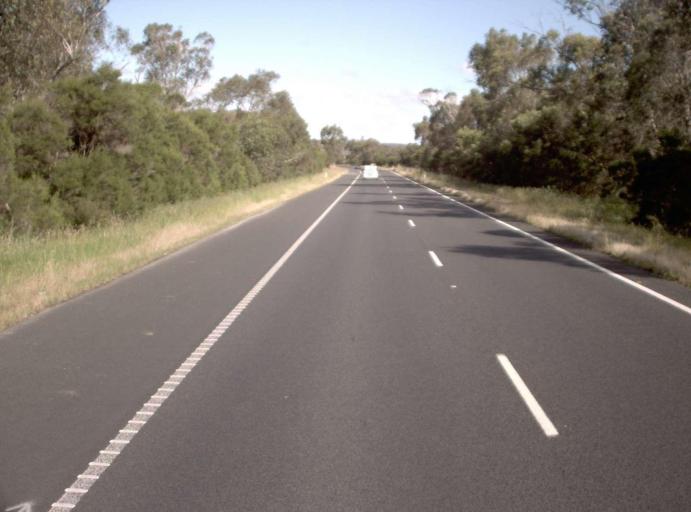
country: AU
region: Victoria
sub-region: Cardinia
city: Koo-Wee-Rup
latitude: -38.3280
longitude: 145.5470
